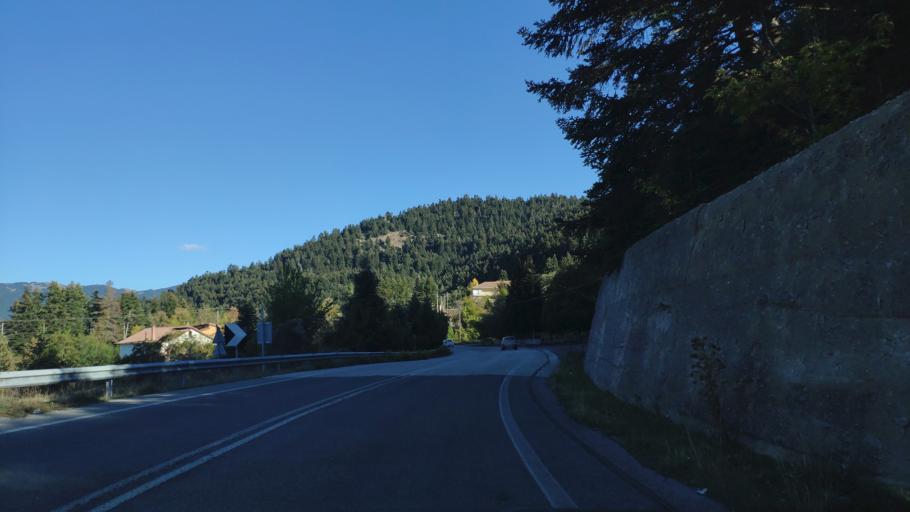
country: GR
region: Peloponnese
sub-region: Nomos Arkadias
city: Langadhia
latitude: 37.6564
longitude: 22.1288
